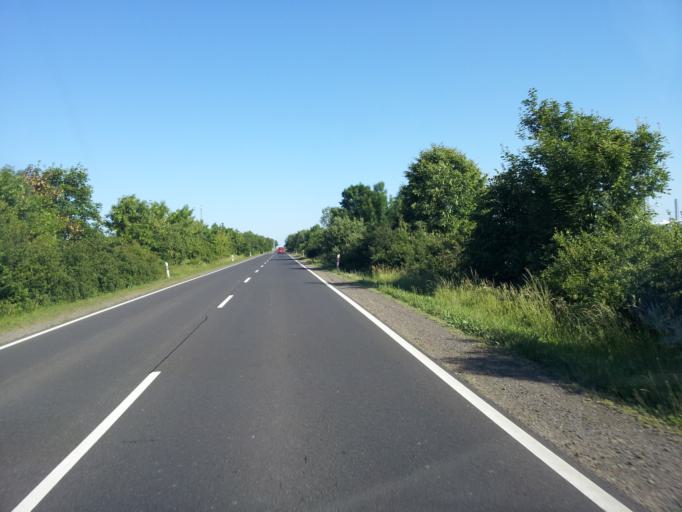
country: HU
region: Nograd
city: Nagyoroszi
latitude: 47.9885
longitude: 19.1095
